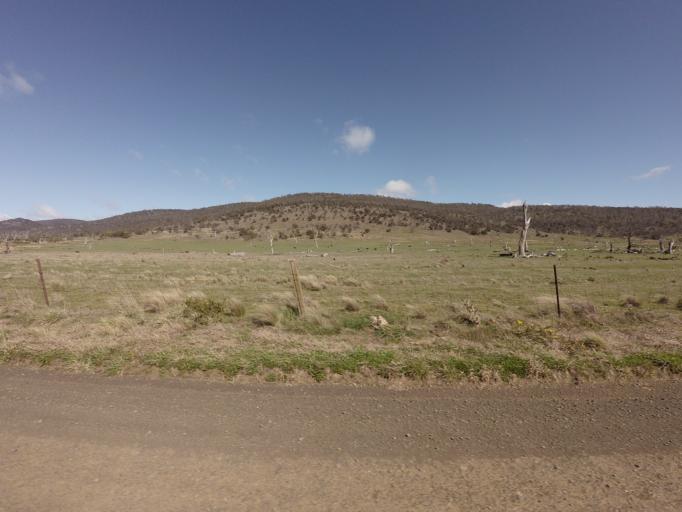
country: AU
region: Tasmania
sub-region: Northern Midlands
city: Evandale
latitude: -41.9274
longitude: 147.4118
